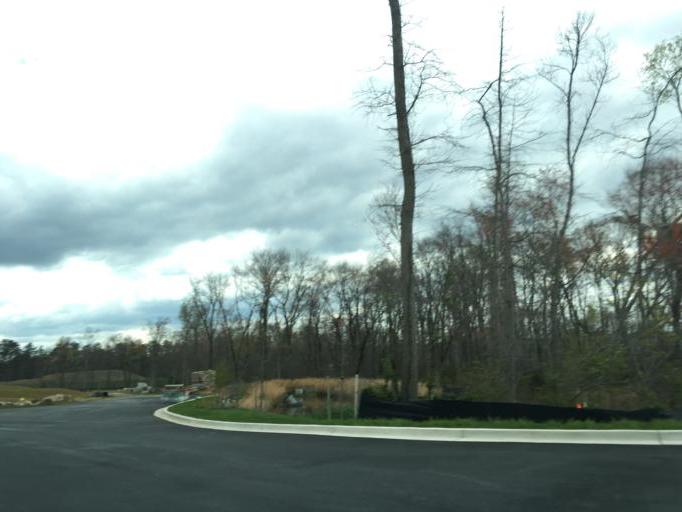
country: US
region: Maryland
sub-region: Howard County
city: Hanover
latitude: 39.1809
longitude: -76.7151
